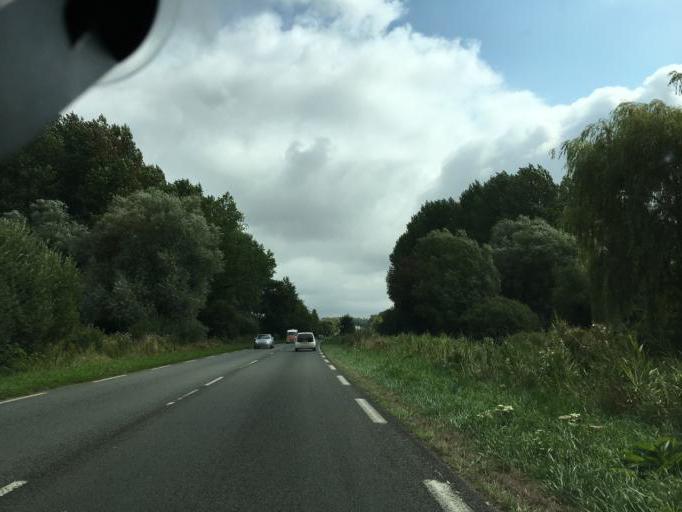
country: FR
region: Nord-Pas-de-Calais
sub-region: Departement du Pas-de-Calais
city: Verton
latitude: 50.4077
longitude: 1.6400
